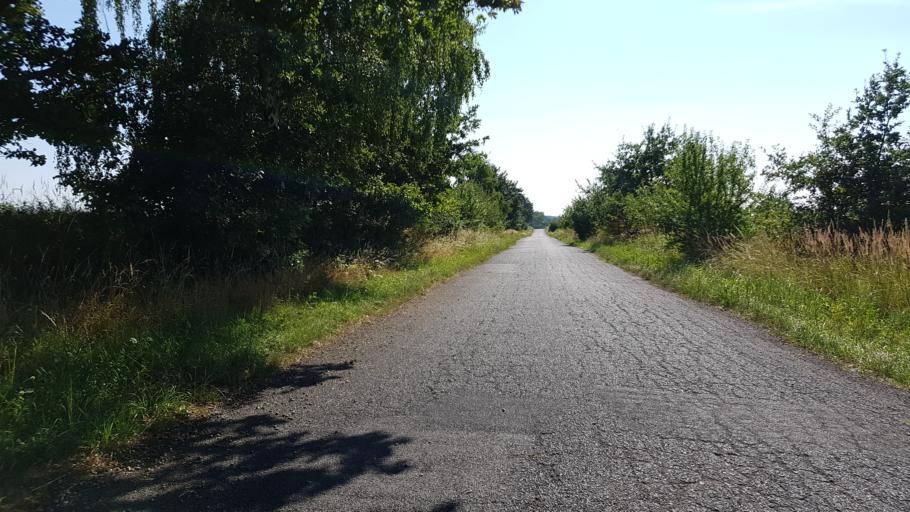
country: PL
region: West Pomeranian Voivodeship
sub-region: Powiat gryfinski
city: Gryfino
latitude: 53.1539
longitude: 14.5192
